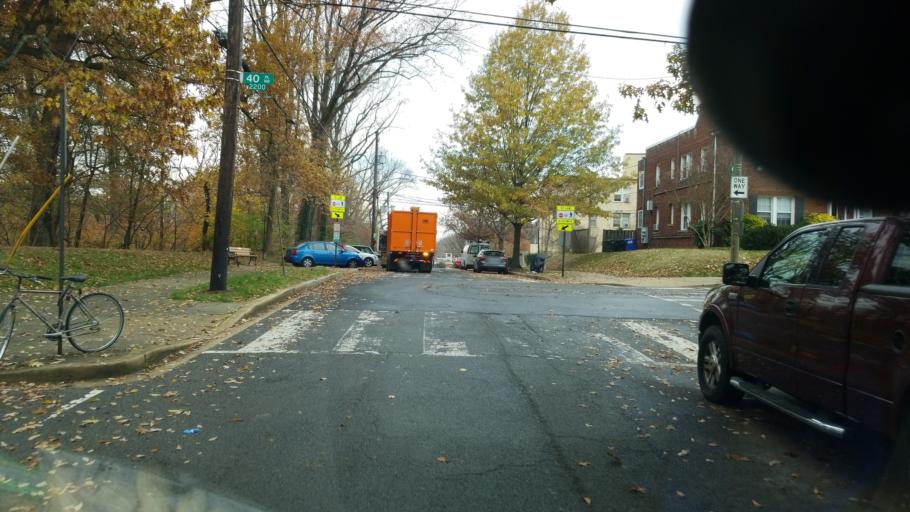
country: US
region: Maryland
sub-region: Montgomery County
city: Friendship Village
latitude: 38.9191
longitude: -77.0793
